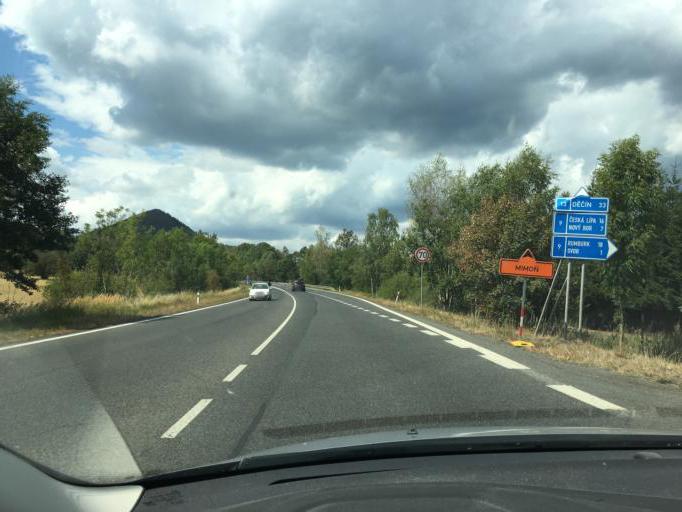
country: CZ
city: Cvikov
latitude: 50.7895
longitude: 14.6045
